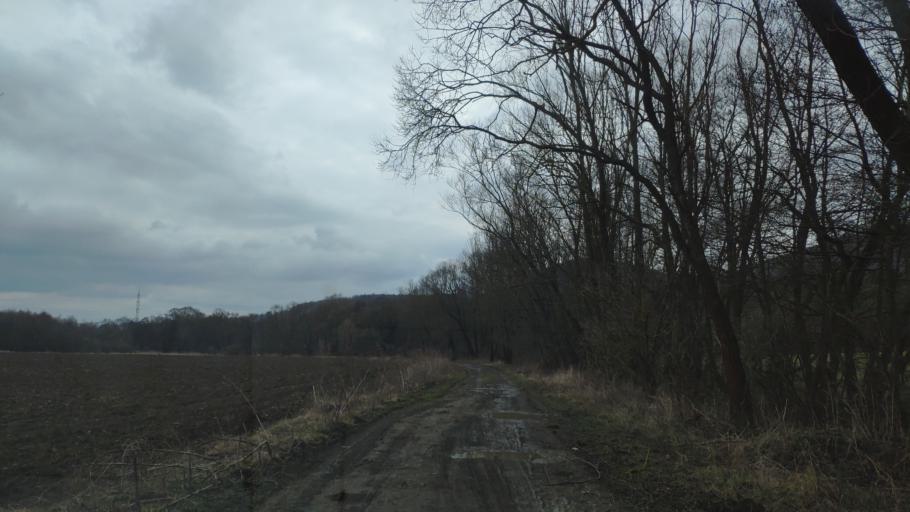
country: SK
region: Presovsky
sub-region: Okres Presov
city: Presov
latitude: 49.0771
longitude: 21.2893
